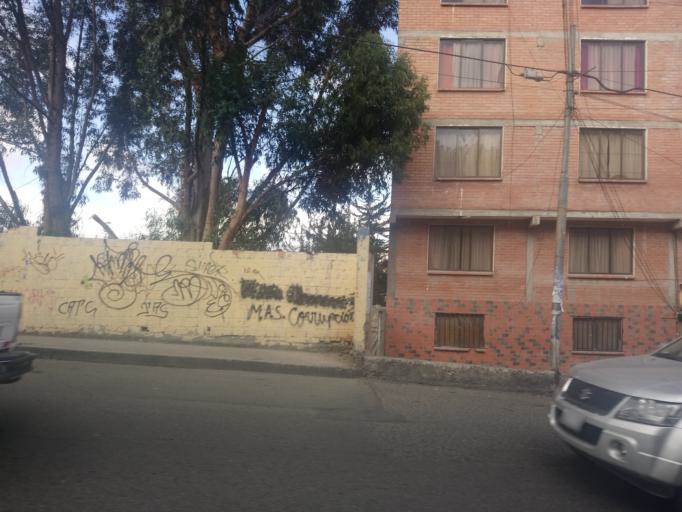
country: BO
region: La Paz
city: La Paz
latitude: -16.4965
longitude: -68.1117
